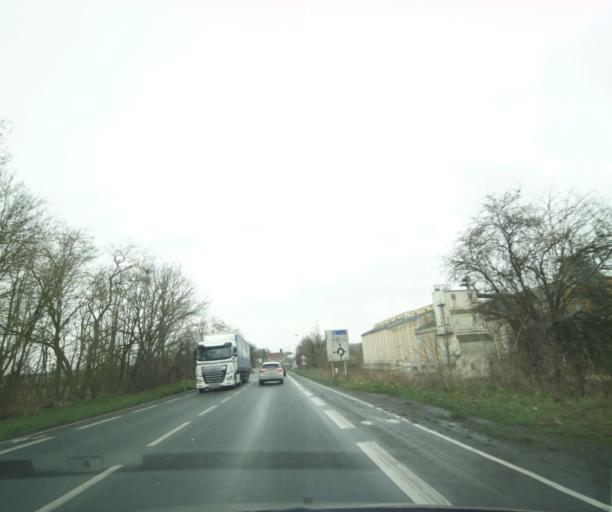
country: FR
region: Nord-Pas-de-Calais
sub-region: Departement du Nord
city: Haulchin
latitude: 50.3227
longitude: 3.4319
